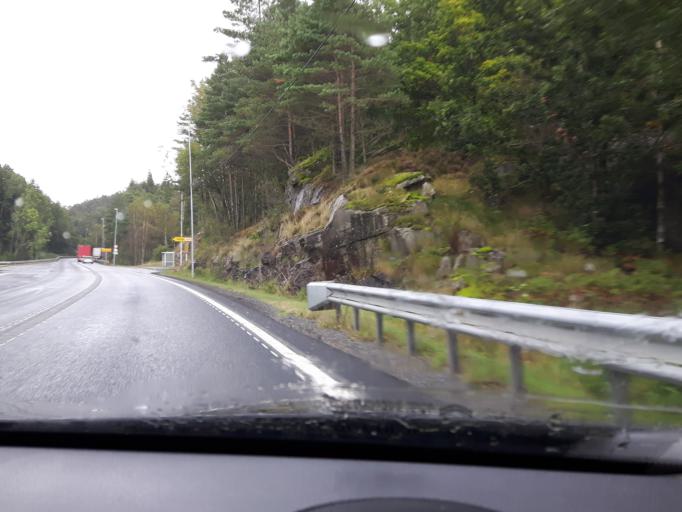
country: NO
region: Vest-Agder
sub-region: Marnardal
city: Helland
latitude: 58.0923
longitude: 7.6285
